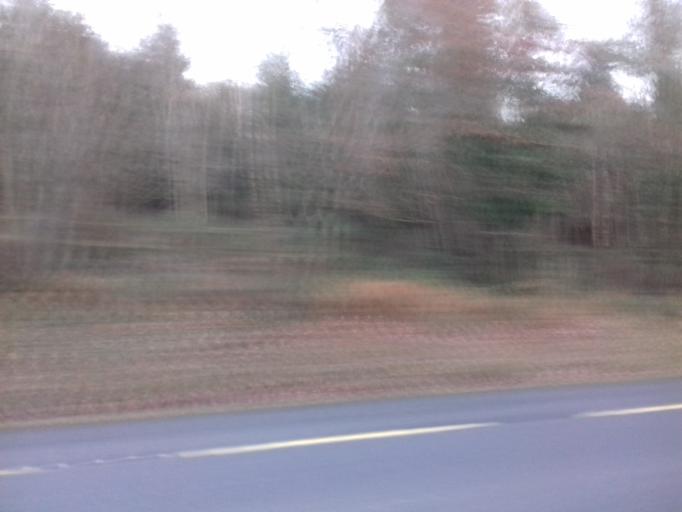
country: IE
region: Ulster
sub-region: County Monaghan
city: Monaghan
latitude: 54.2358
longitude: -6.8731
